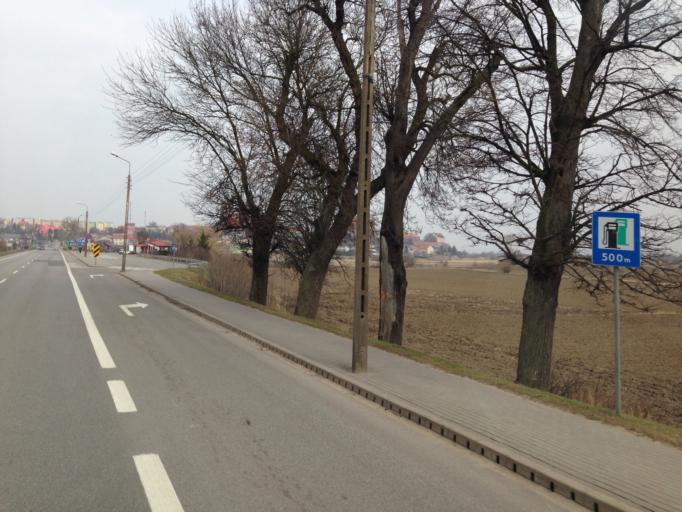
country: PL
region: Pomeranian Voivodeship
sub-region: Powiat tczewski
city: Gniew
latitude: 53.8283
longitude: 18.8161
